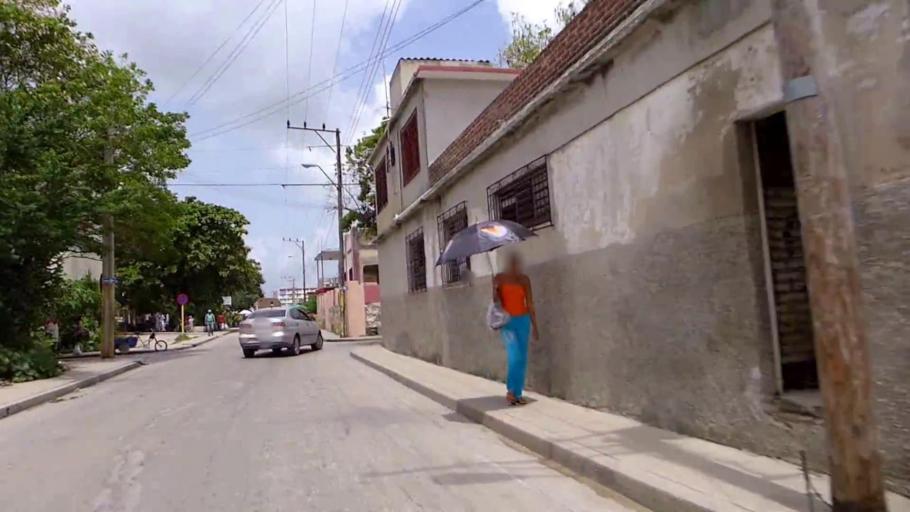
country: CU
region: Holguin
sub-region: Municipio de Holguin
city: Holguin
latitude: 20.8892
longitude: -76.2650
